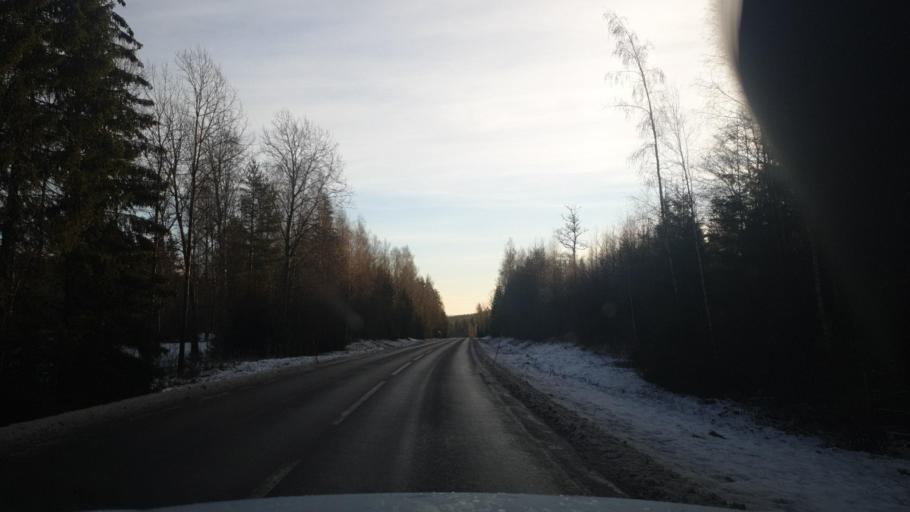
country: SE
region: Vaermland
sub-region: Arvika Kommun
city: Arvika
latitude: 59.6448
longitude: 12.7808
